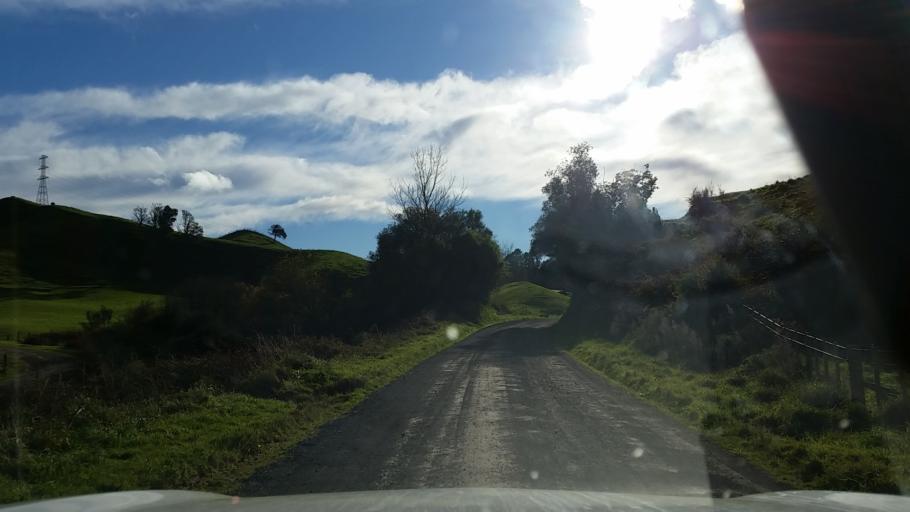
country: NZ
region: Waikato
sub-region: South Waikato District
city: Tokoroa
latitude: -38.3716
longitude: 176.0864
